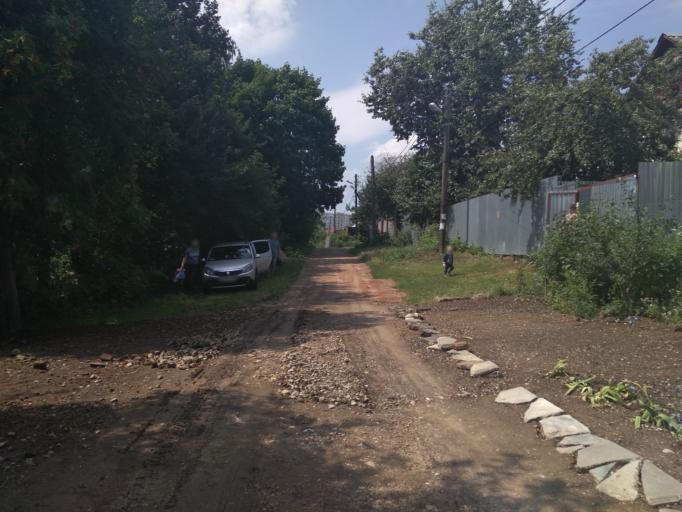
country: RU
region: Tula
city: Mendeleyevskiy
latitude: 54.1620
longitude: 37.6098
